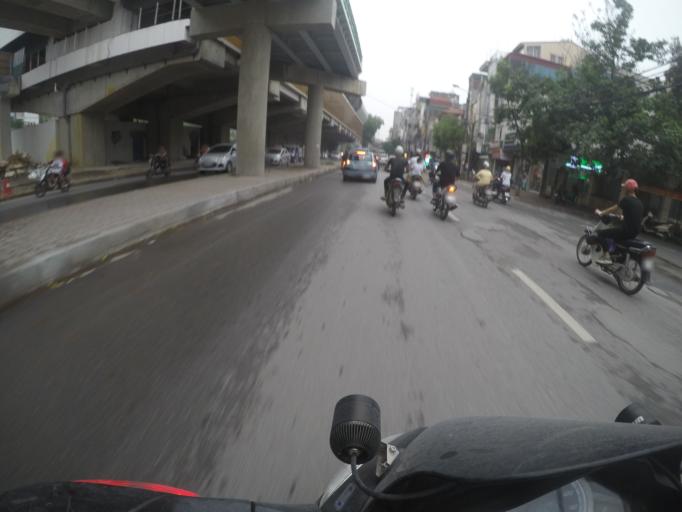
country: VN
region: Ha Noi
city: Dong Da
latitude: 21.0060
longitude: 105.8166
